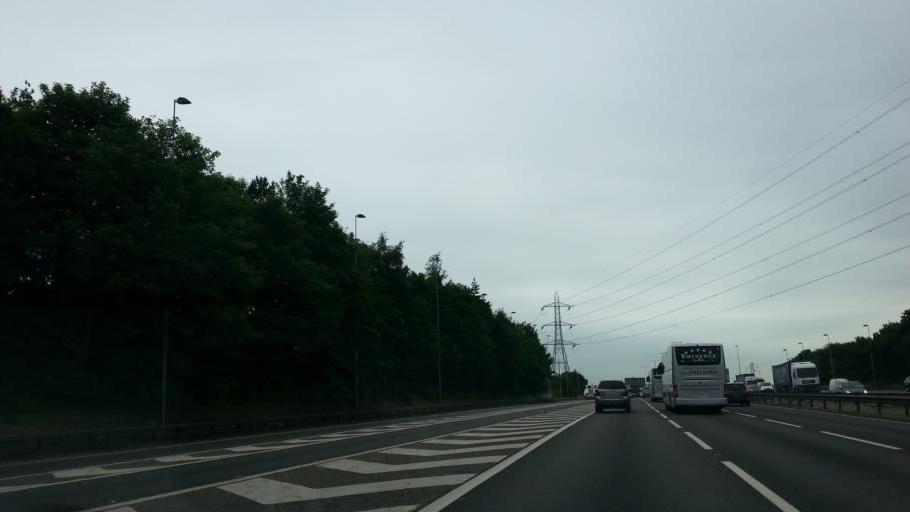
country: GB
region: England
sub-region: Solihull
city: Bickenhill
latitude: 52.4422
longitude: -1.7114
